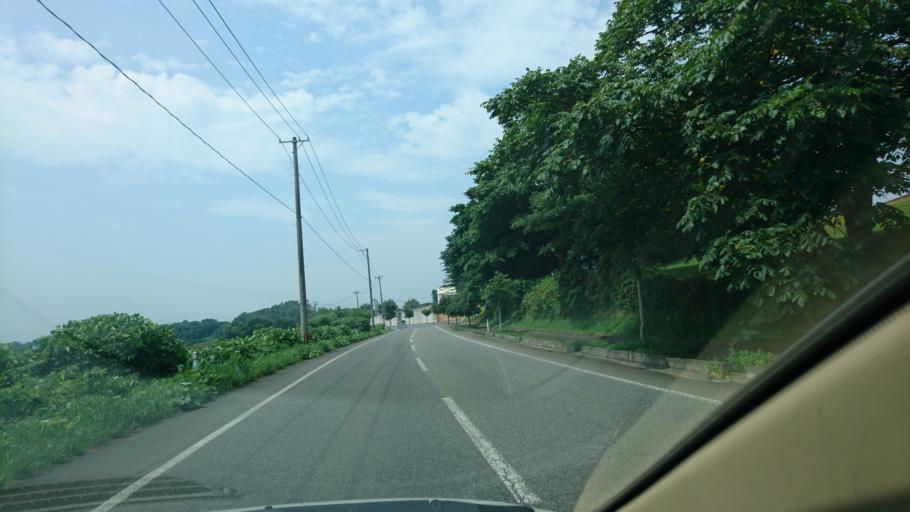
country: JP
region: Iwate
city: Kitakami
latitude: 39.2560
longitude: 141.0868
